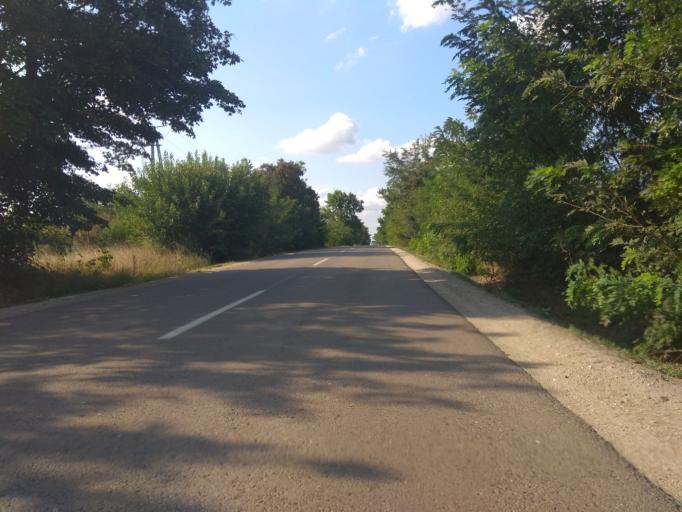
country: HU
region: Borsod-Abauj-Zemplen
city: Hejobaba
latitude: 47.8947
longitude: 20.8931
